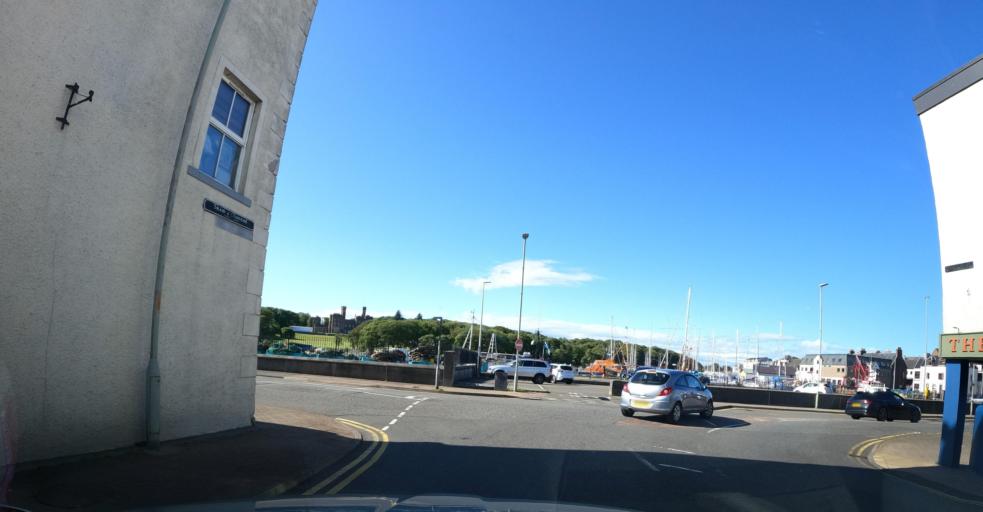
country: GB
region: Scotland
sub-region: Eilean Siar
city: Stornoway
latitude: 58.2083
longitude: -6.3905
